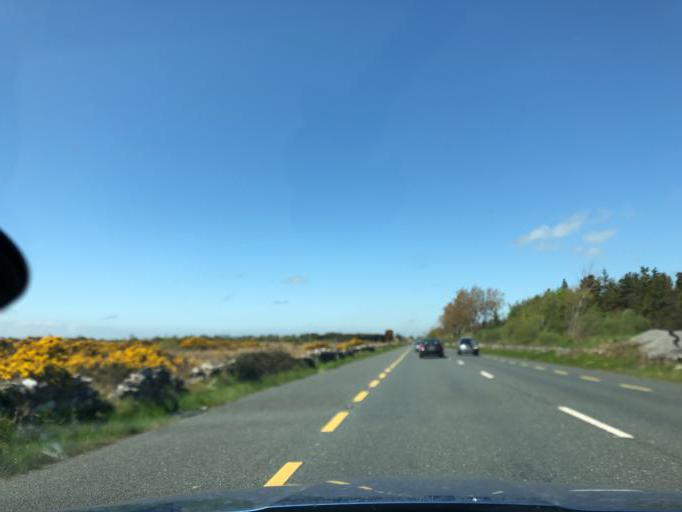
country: IE
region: Connaught
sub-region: County Galway
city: Loughrea
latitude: 53.2071
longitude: -8.6188
